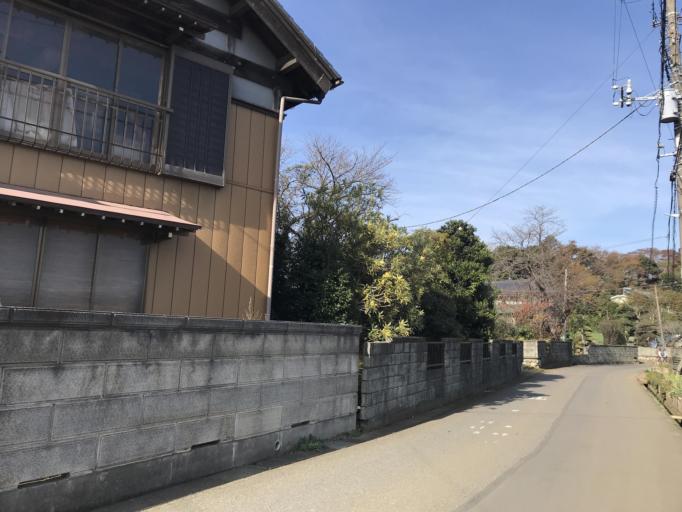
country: JP
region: Chiba
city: Shiroi
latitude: 35.7842
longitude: 139.9938
